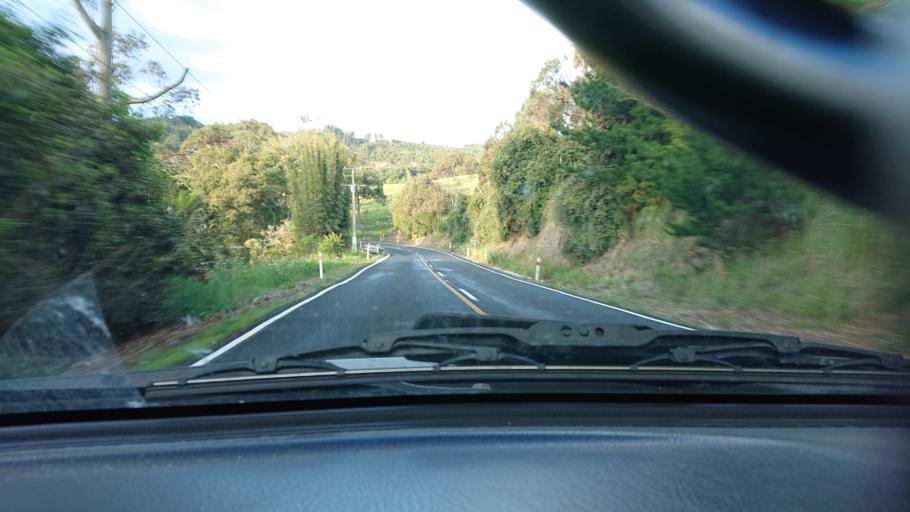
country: NZ
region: Auckland
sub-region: Auckland
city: Parakai
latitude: -36.5366
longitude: 174.4564
